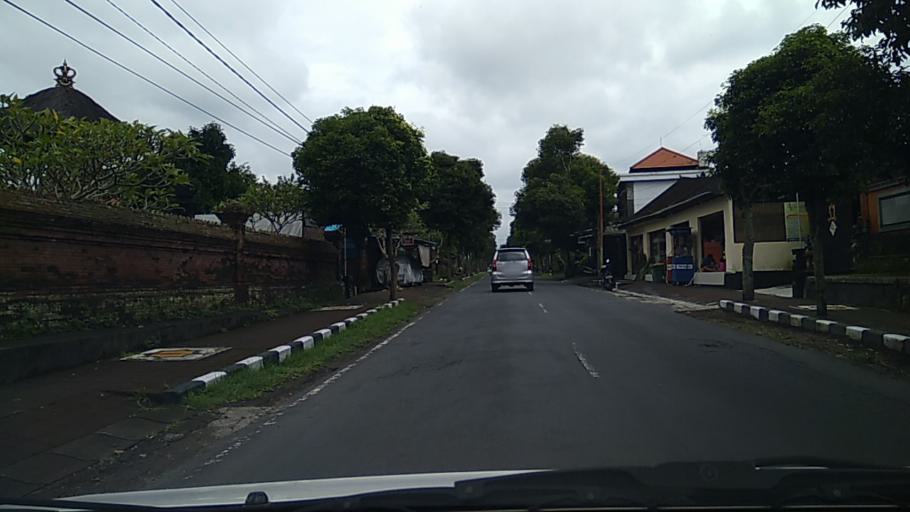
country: ID
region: Bali
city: Brahmana
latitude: -8.4847
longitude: 115.2102
